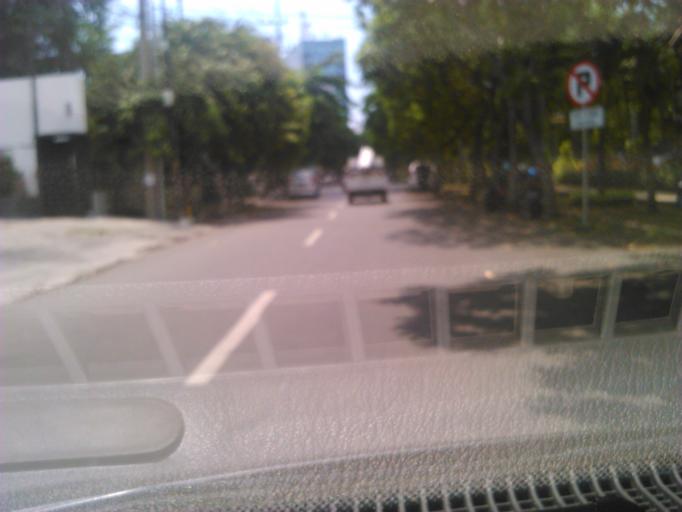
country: ID
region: East Java
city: Gubengairlangga
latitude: -7.2685
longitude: 112.7392
